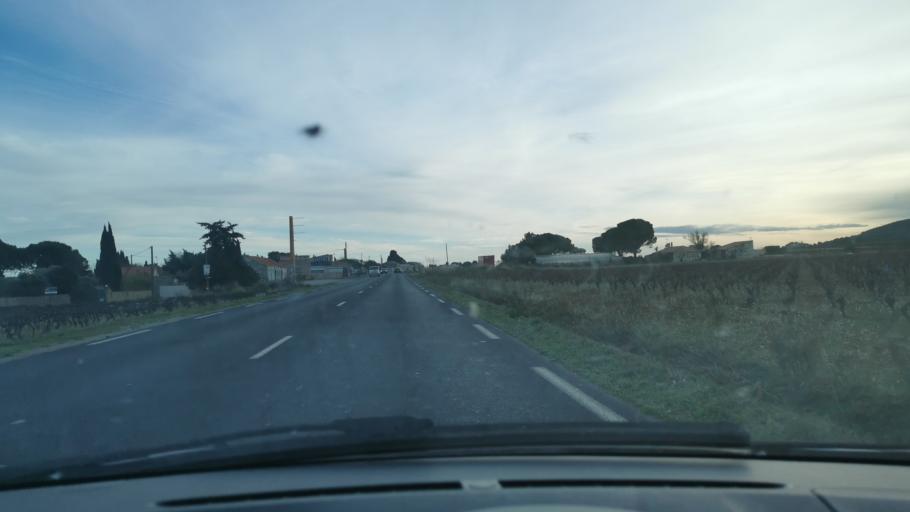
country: FR
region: Languedoc-Roussillon
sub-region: Departement de l'Herault
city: Vic-la-Gardiole
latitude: 43.4859
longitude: 3.7725
